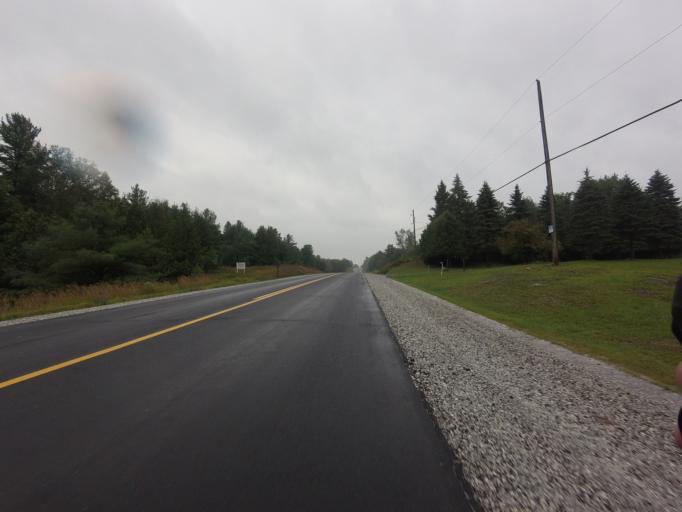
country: CA
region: Ontario
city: Perth
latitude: 45.0892
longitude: -76.4541
